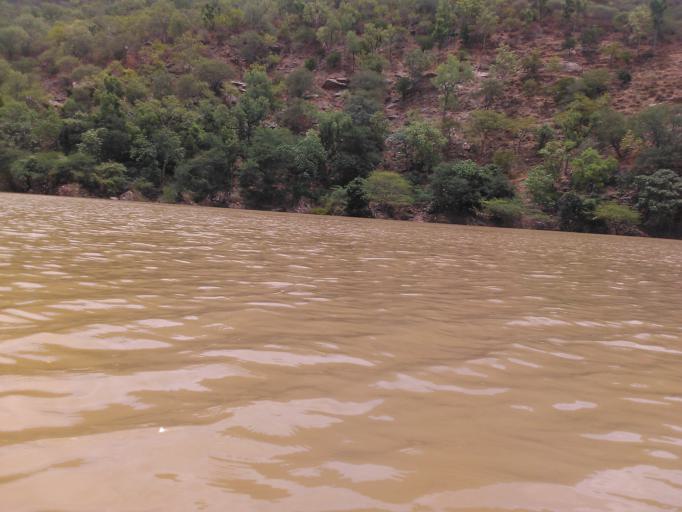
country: IN
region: Tamil Nadu
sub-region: Dharmapuri
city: Pennagaram
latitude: 12.1115
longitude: 77.7781
